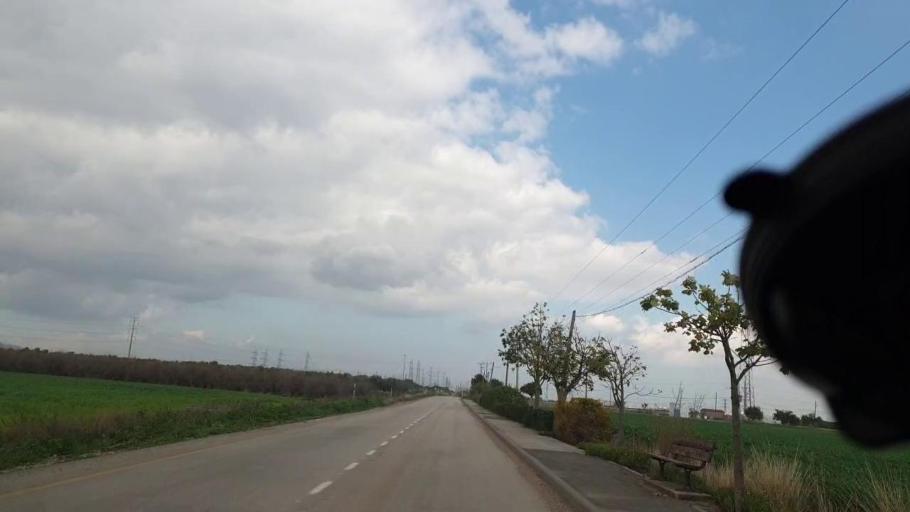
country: IL
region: Haifa
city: Rekhasim
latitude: 32.7527
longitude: 35.0868
